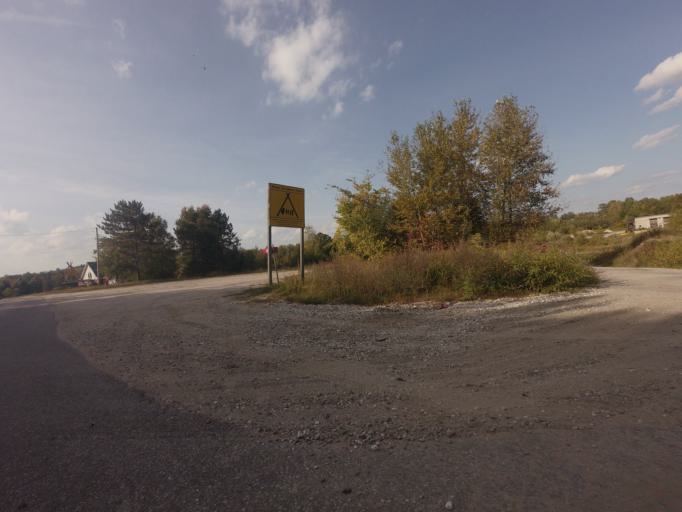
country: CA
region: Quebec
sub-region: Outaouais
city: Maniwaki
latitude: 46.3638
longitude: -75.9875
